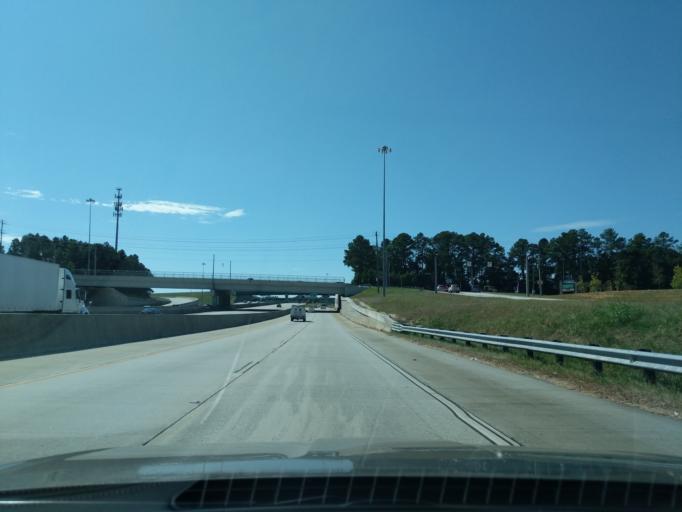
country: US
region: Georgia
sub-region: Columbia County
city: Martinez
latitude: 33.4958
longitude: -82.0784
